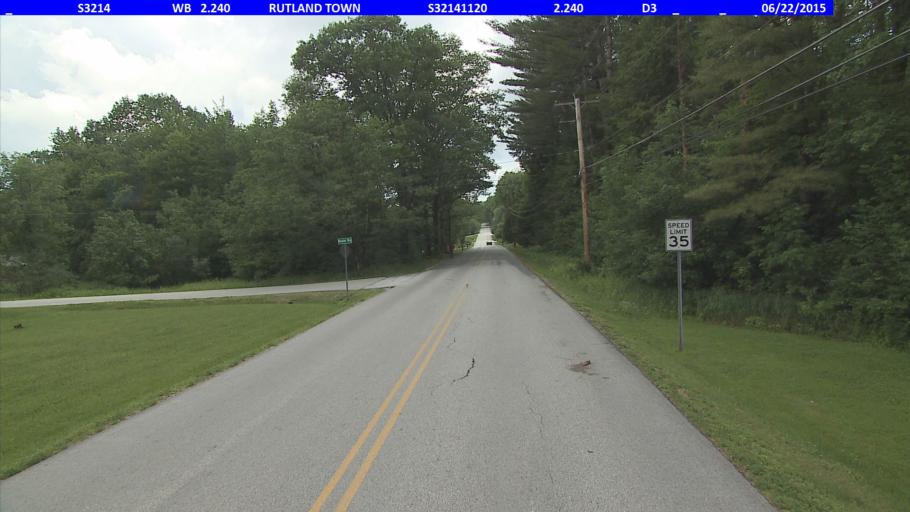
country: US
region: Vermont
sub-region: Rutland County
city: Rutland
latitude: 43.6330
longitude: -72.9435
